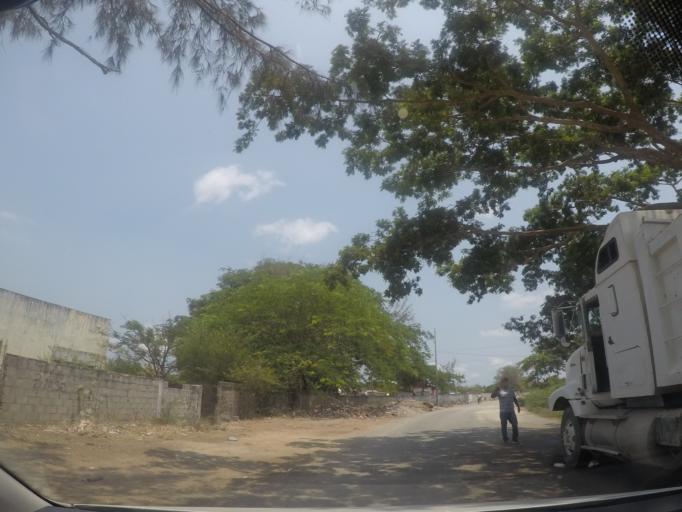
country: MX
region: Oaxaca
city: Asuncion Ixtaltepec
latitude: 16.5052
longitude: -95.0662
